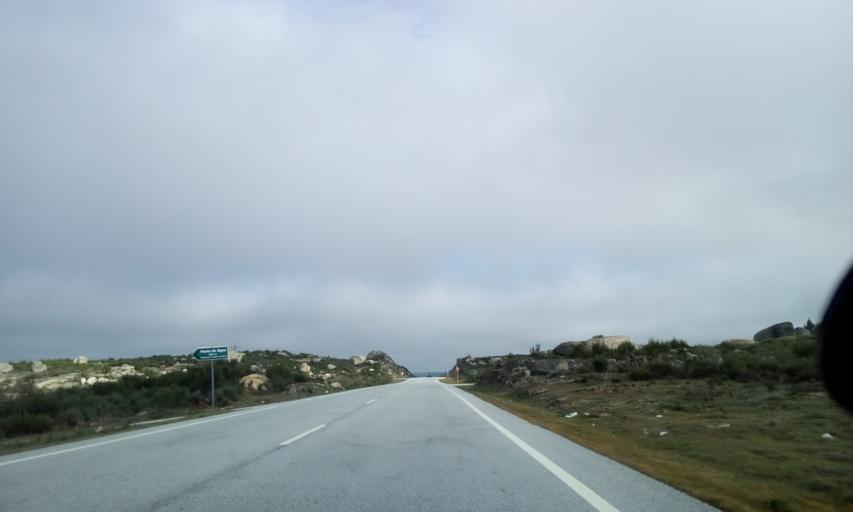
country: PT
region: Guarda
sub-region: Aguiar da Beira
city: Aguiar da Beira
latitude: 40.7650
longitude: -7.5024
